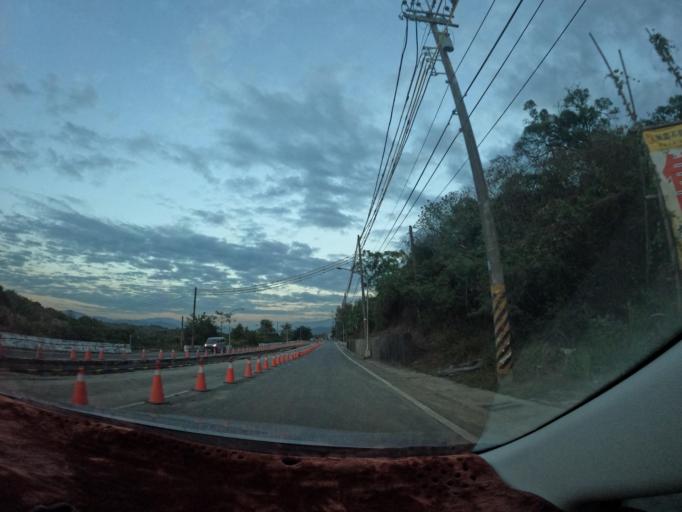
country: TW
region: Taiwan
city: Yujing
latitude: 23.0960
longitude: 120.4406
